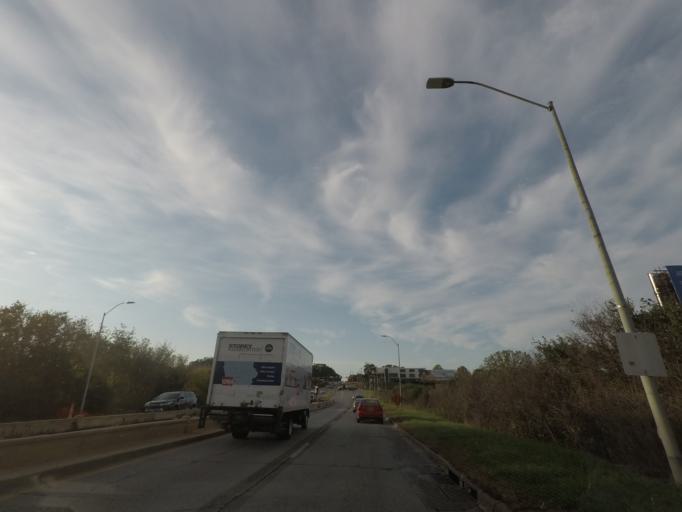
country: US
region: Iowa
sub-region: Polk County
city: Des Moines
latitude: 41.5648
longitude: -93.6451
